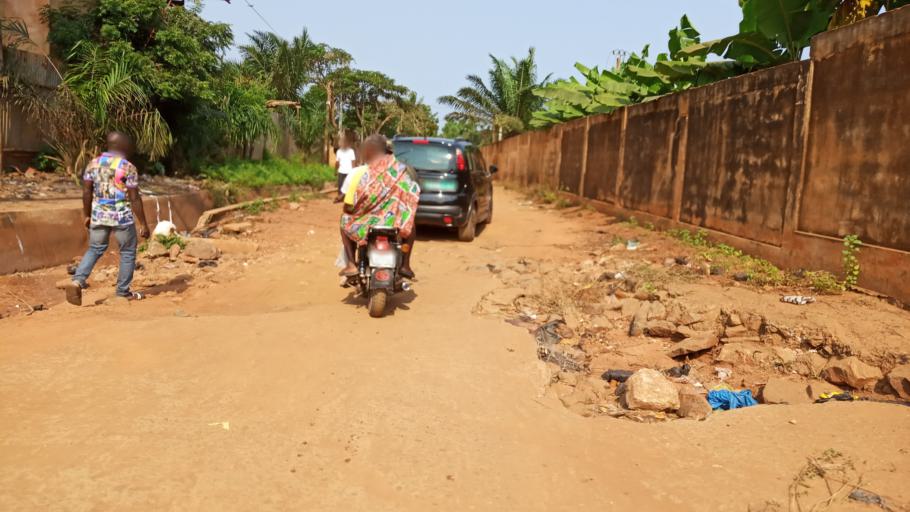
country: TG
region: Maritime
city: Lome
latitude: 6.2079
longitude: 1.2032
